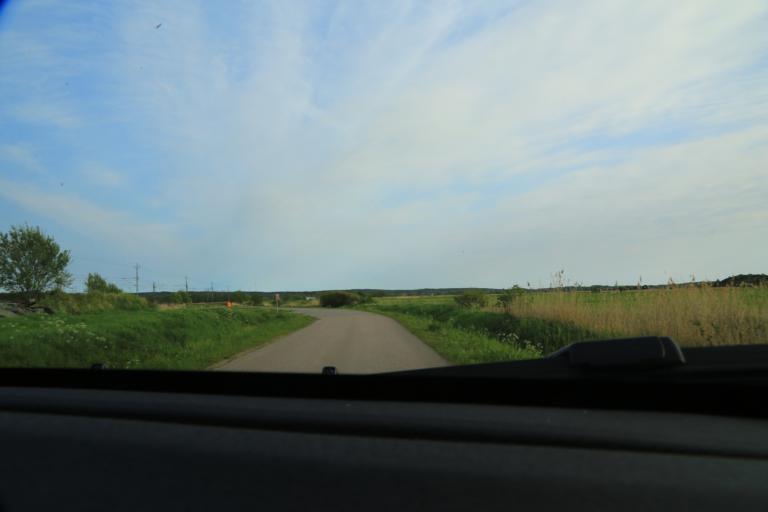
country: SE
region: Halland
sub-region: Kungsbacka Kommun
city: Frillesas
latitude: 57.2336
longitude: 12.2032
